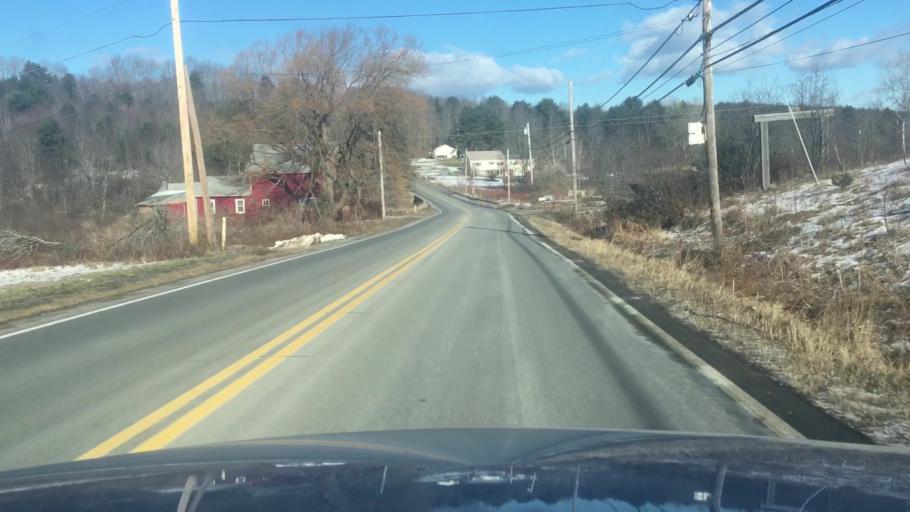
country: US
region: Maine
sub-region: Somerset County
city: Fairfield
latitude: 44.6489
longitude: -69.6760
